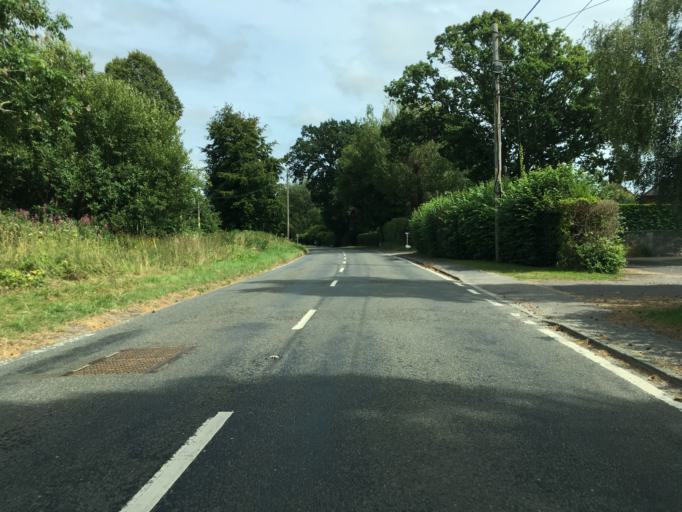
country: GB
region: England
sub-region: East Sussex
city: Crowborough
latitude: 51.1111
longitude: 0.1723
